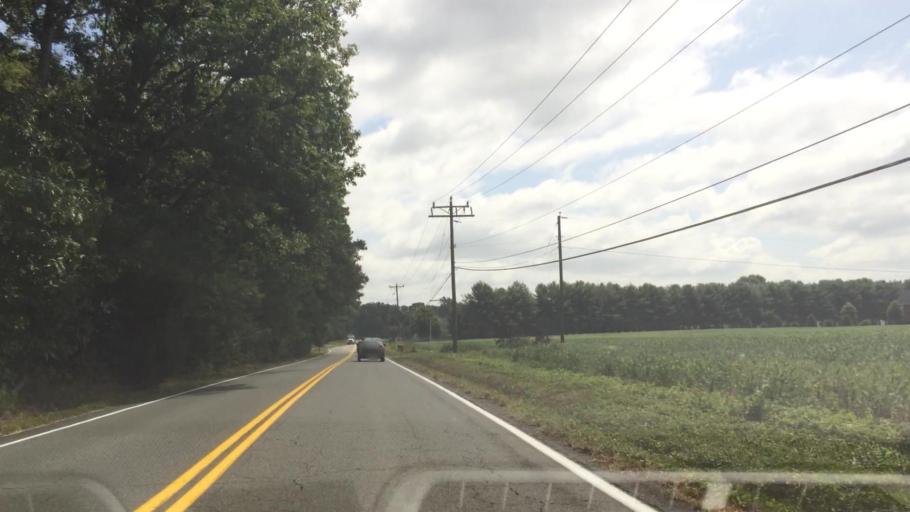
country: US
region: Virginia
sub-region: Henrico County
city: Chamberlayne
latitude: 37.6864
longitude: -77.4355
